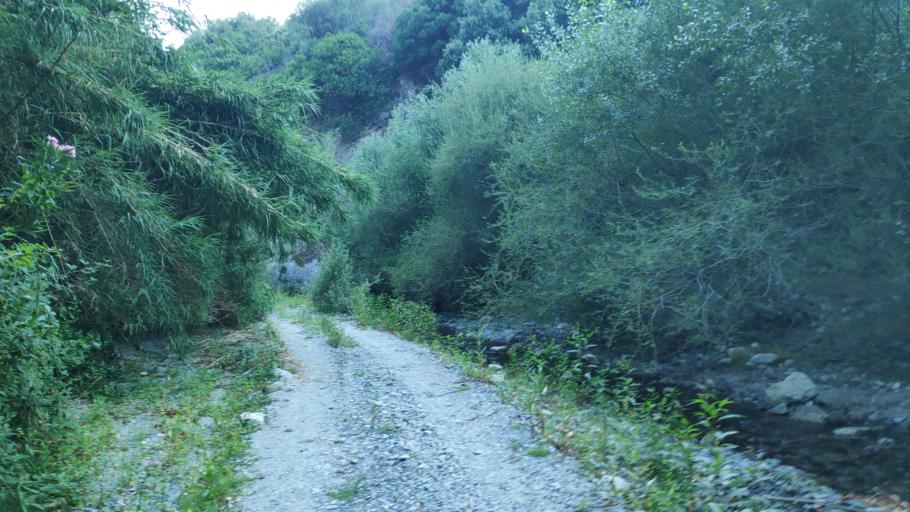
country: IT
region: Calabria
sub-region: Provincia di Reggio Calabria
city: Placanica
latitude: 38.4163
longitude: 16.4368
